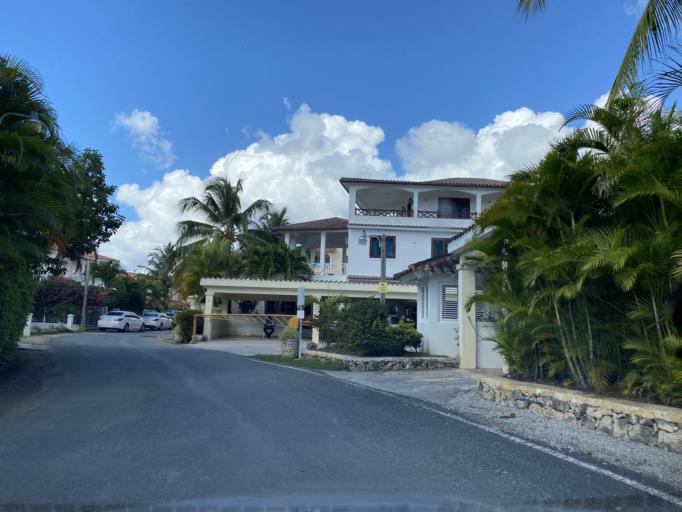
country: DO
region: La Romana
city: La Romana
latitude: 18.3497
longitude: -68.8264
